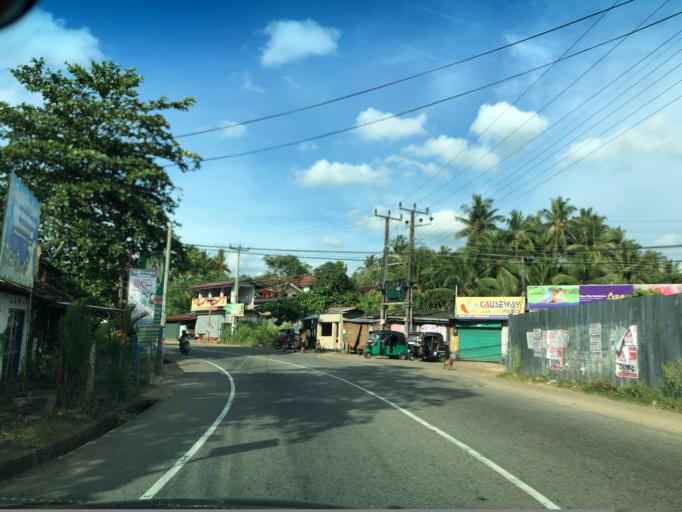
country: LK
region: Western
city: Horawala Junction
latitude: 6.5265
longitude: 80.0929
